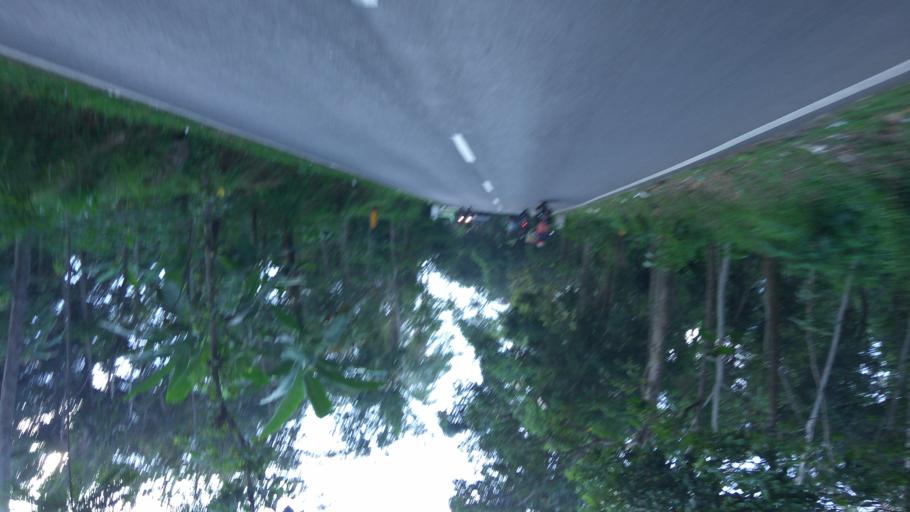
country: ID
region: Central Java
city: Salatiga
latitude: -7.3661
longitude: 110.4708
